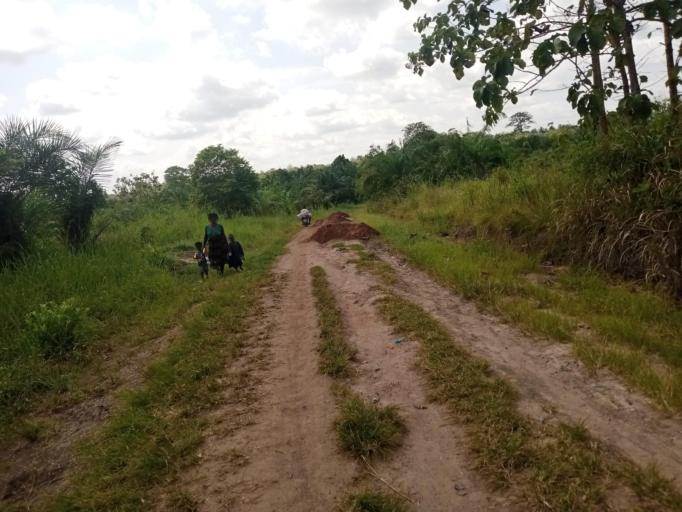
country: TG
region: Maritime
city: Tsevie
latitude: 6.5215
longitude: 1.0548
